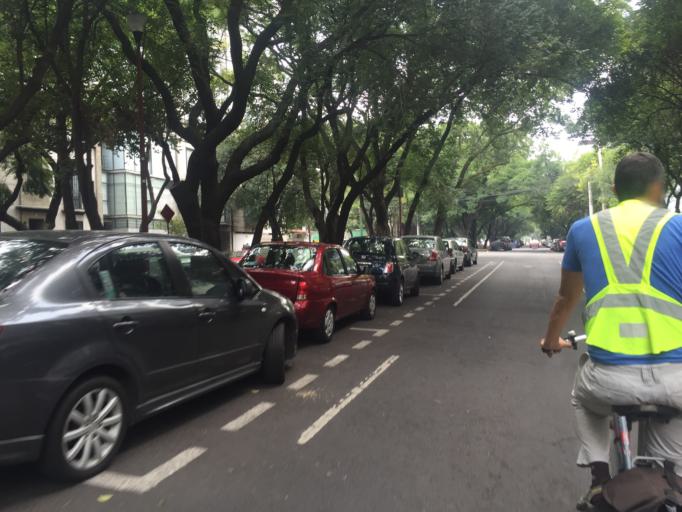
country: MX
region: Mexico City
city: Benito Juarez
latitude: 19.4166
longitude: -99.1729
